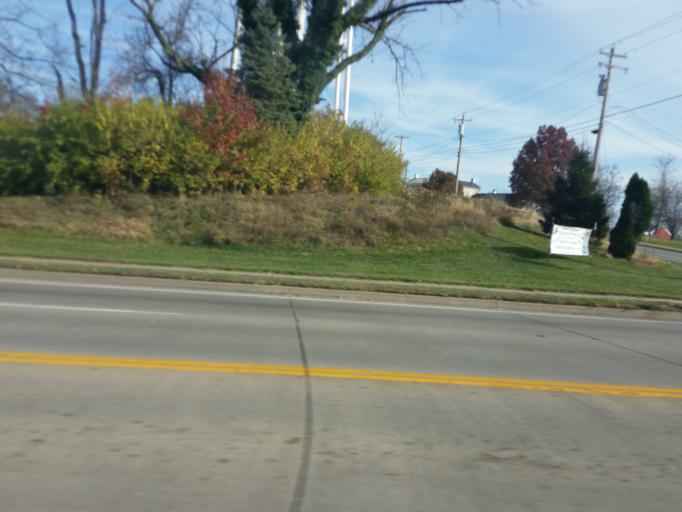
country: US
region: Kentucky
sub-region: Campbell County
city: Alexandria
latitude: 38.9581
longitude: -84.3931
